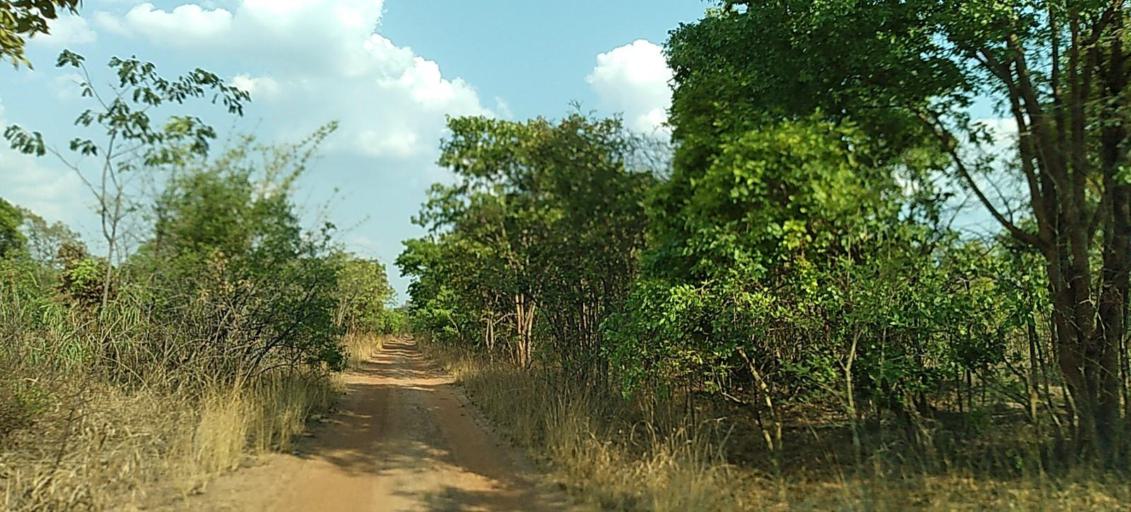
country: ZM
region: Copperbelt
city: Luanshya
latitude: -13.1638
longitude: 28.3434
